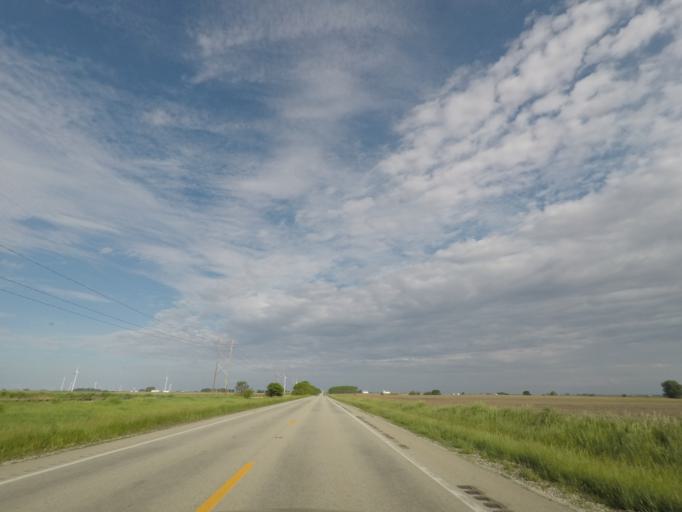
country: US
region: Illinois
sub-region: Logan County
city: Mount Pulaski
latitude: 39.9769
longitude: -89.1970
